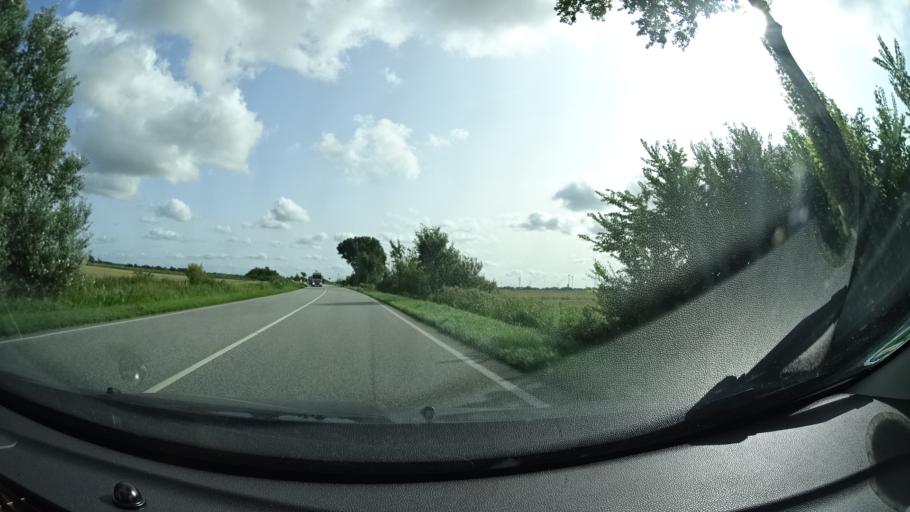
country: DE
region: Schleswig-Holstein
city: Stelle-Wittenwurth
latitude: 54.2387
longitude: 9.0360
